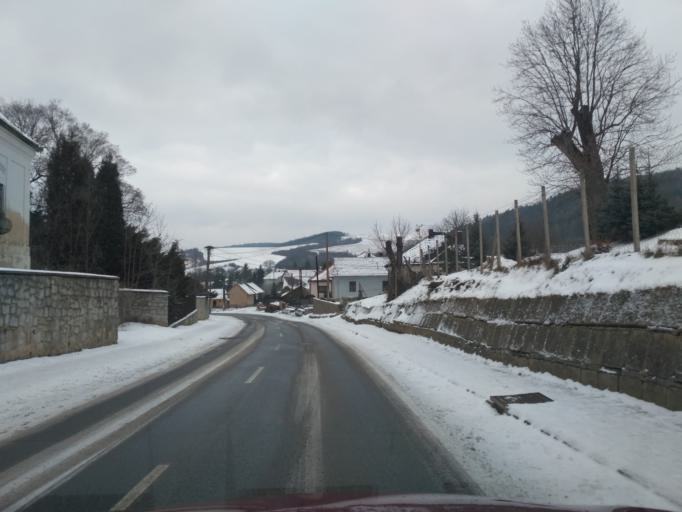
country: SK
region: Presovsky
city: Sabinov
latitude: 49.0112
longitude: 21.1246
